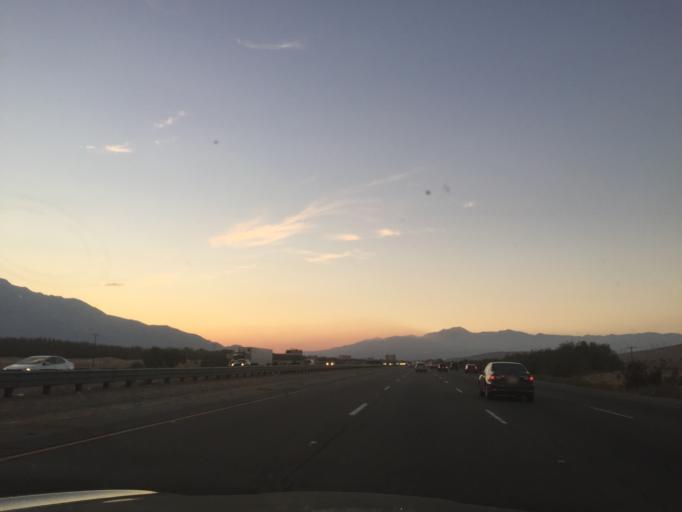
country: US
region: California
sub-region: Riverside County
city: Thousand Palms
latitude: 33.8272
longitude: -116.4206
